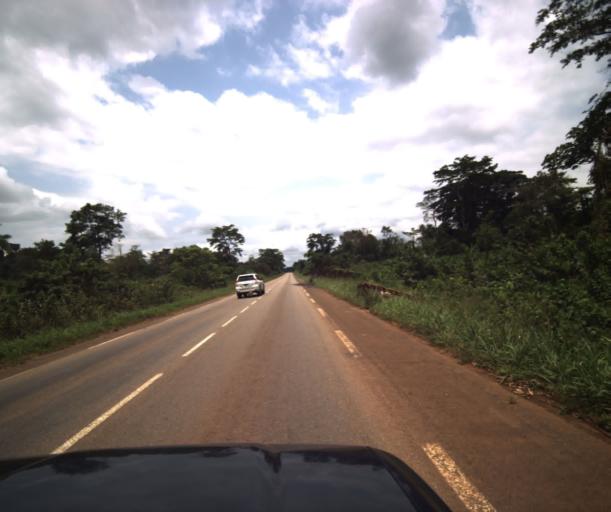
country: CM
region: Centre
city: Eseka
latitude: 3.8546
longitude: 10.9403
